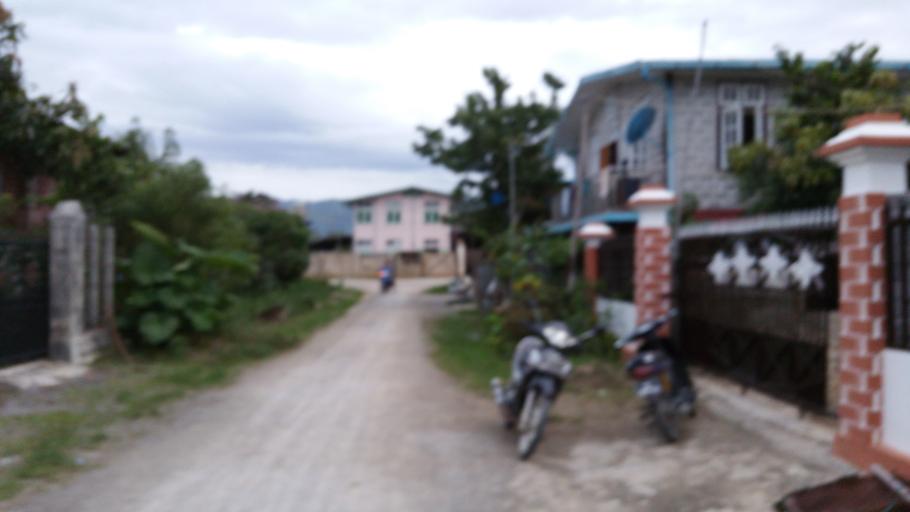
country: MM
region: Shan
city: Taunggyi
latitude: 20.6564
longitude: 96.9285
